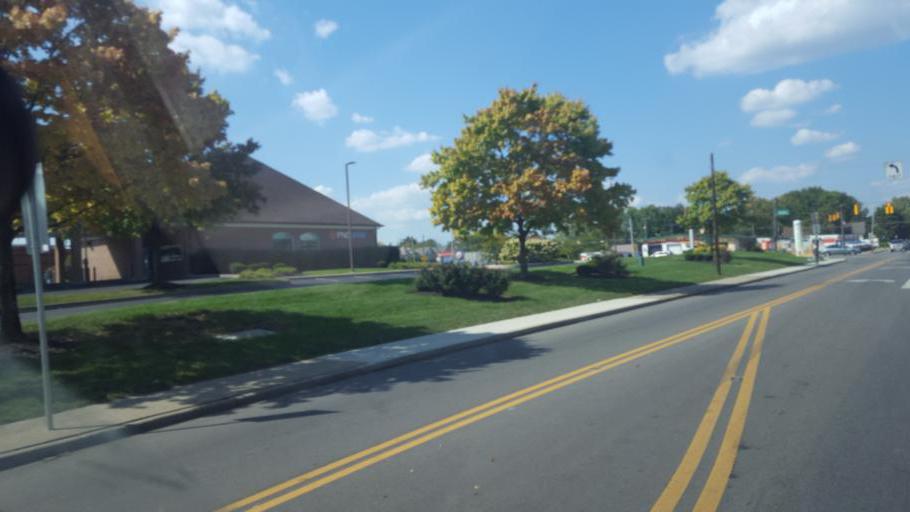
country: US
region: Ohio
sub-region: Franklin County
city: Grandview Heights
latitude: 39.9567
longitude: -83.0379
